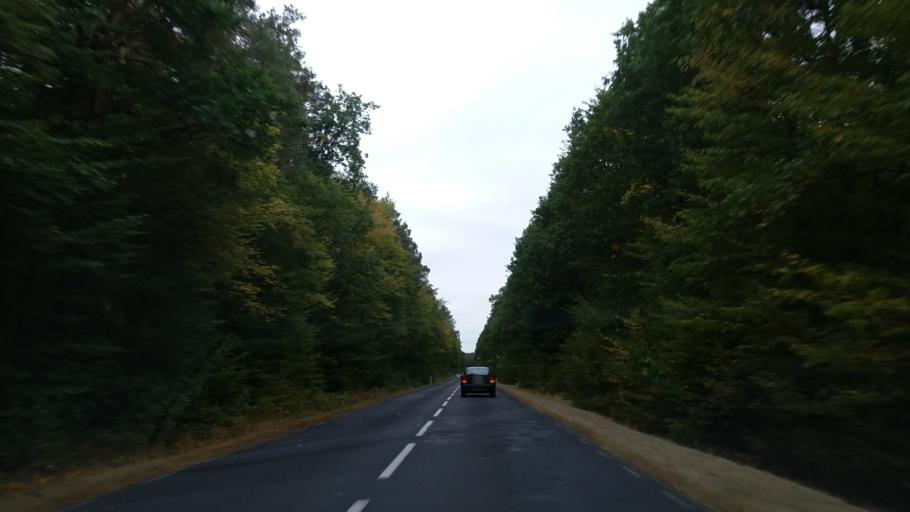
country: PL
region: Lubusz
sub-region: Powiat gorzowski
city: Klodawa
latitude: 52.8530
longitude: 15.1996
